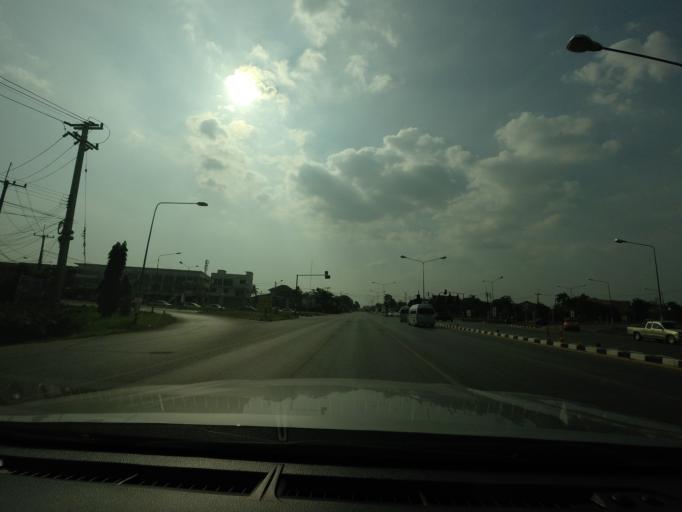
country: TH
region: Sukhothai
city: Sukhothai
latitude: 17.0117
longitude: 99.8375
